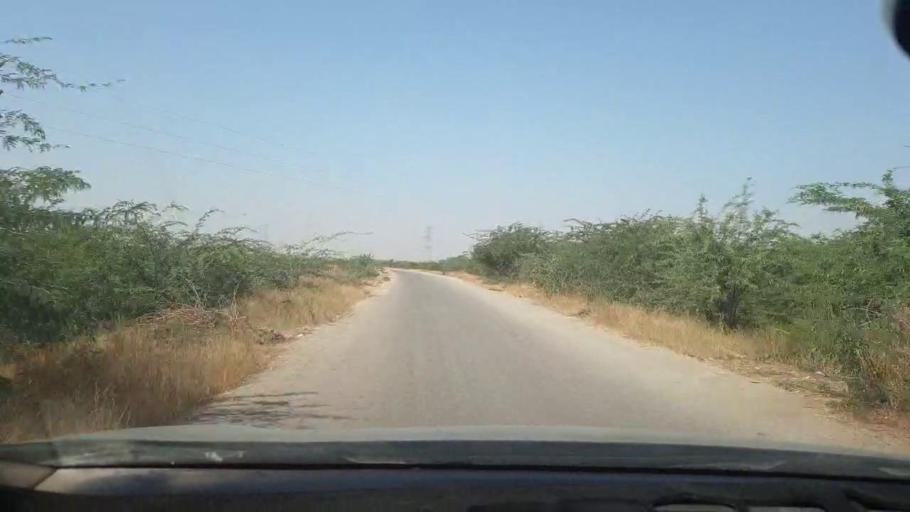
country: PK
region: Sindh
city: Malir Cantonment
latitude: 25.1624
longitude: 67.1539
